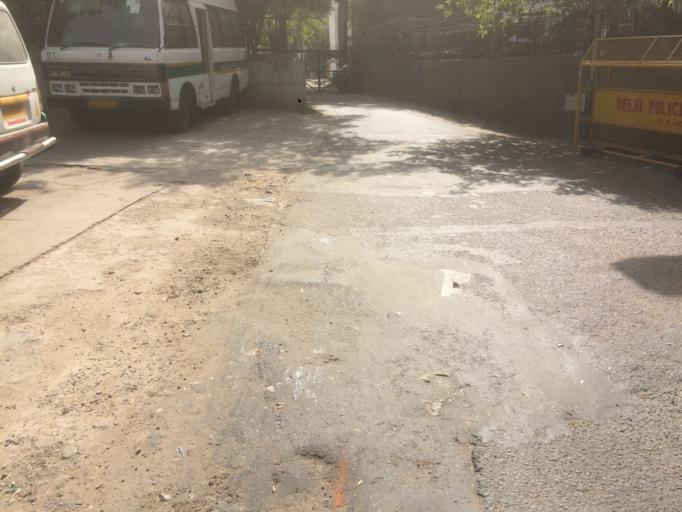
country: IN
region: NCT
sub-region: New Delhi
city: New Delhi
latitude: 28.6300
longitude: 77.2099
